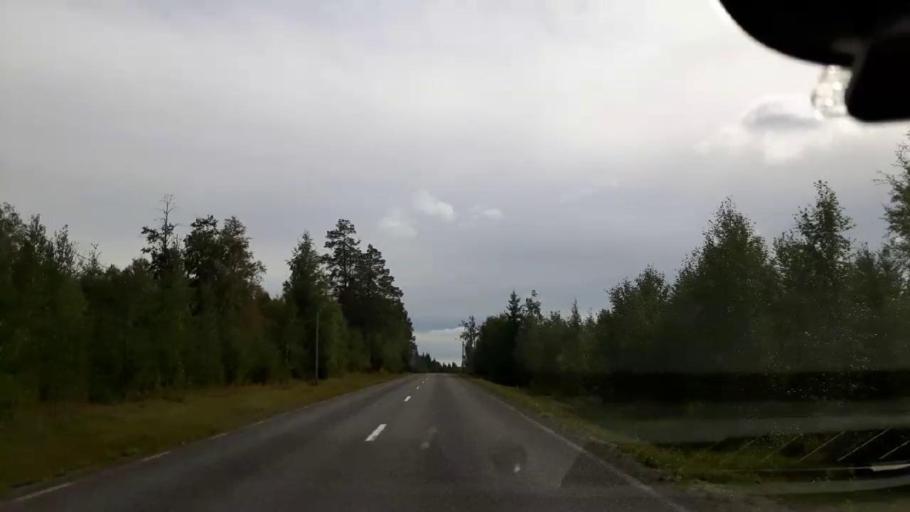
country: SE
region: Jaemtland
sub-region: Ragunda Kommun
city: Hammarstrand
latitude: 63.1350
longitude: 15.8748
